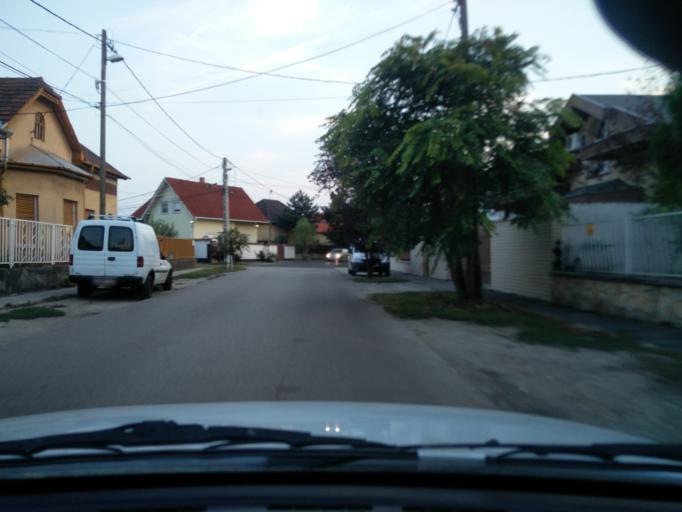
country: HU
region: Budapest
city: Budapest XXI. keruelet
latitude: 47.4143
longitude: 19.0832
